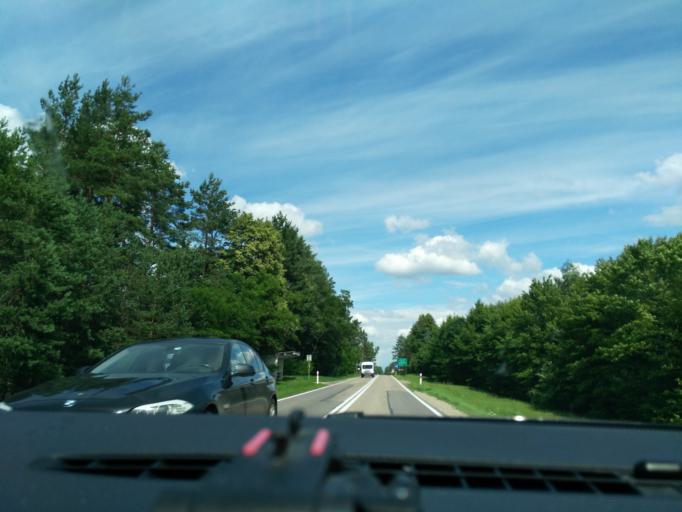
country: PL
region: Podlasie
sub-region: Powiat sejnenski
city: Krasnopol
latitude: 53.9513
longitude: 23.2045
